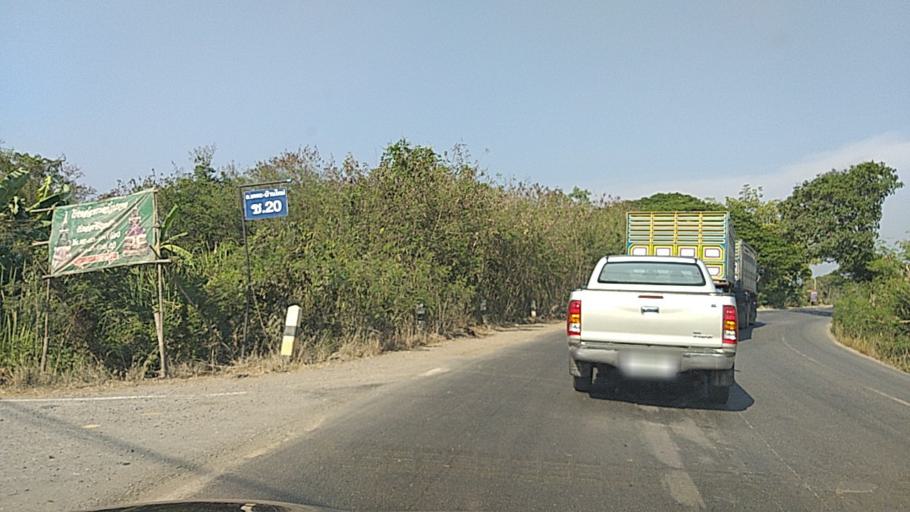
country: TH
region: Nonthaburi
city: Bang Yai
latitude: 13.8791
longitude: 100.3013
